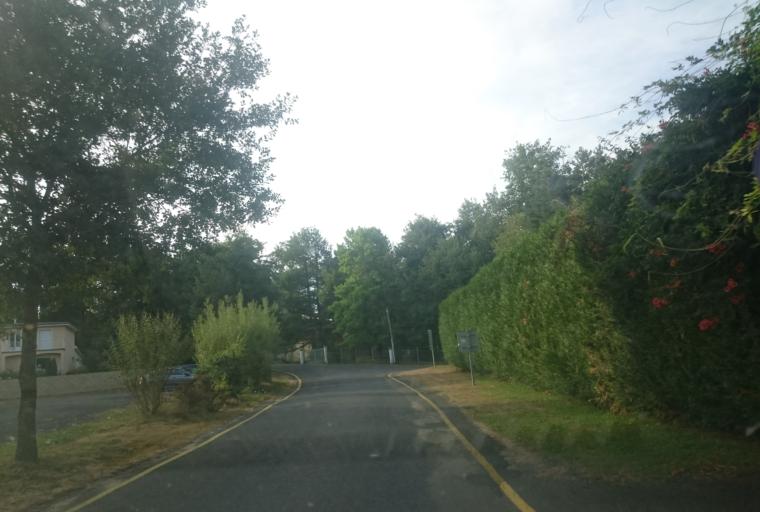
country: FR
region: Auvergne
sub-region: Departement du Cantal
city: Laroquebrou
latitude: 44.9356
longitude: 2.2165
